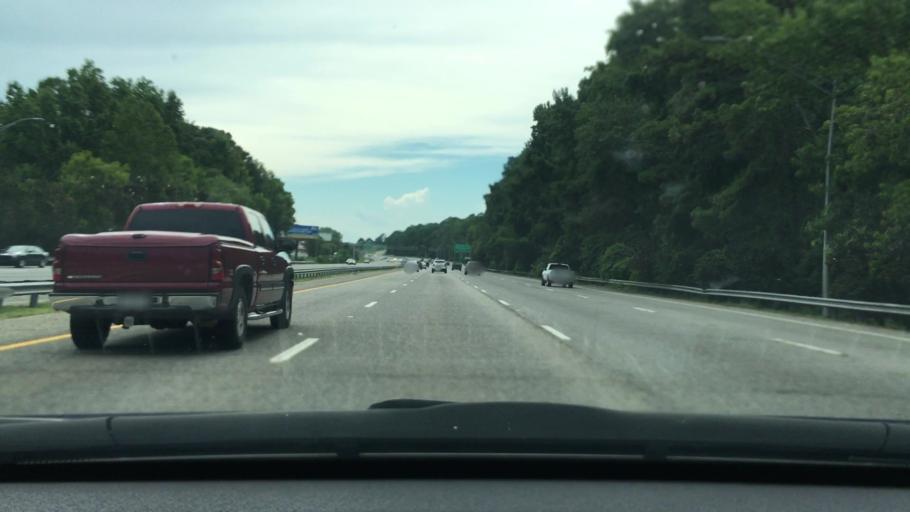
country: US
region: South Carolina
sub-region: Lexington County
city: West Columbia
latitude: 34.0105
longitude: -81.0639
